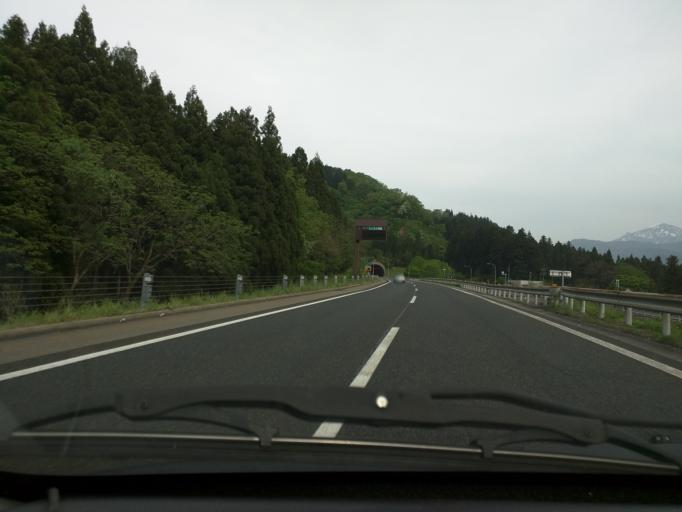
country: JP
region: Niigata
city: Ojiya
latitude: 37.2454
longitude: 138.9415
